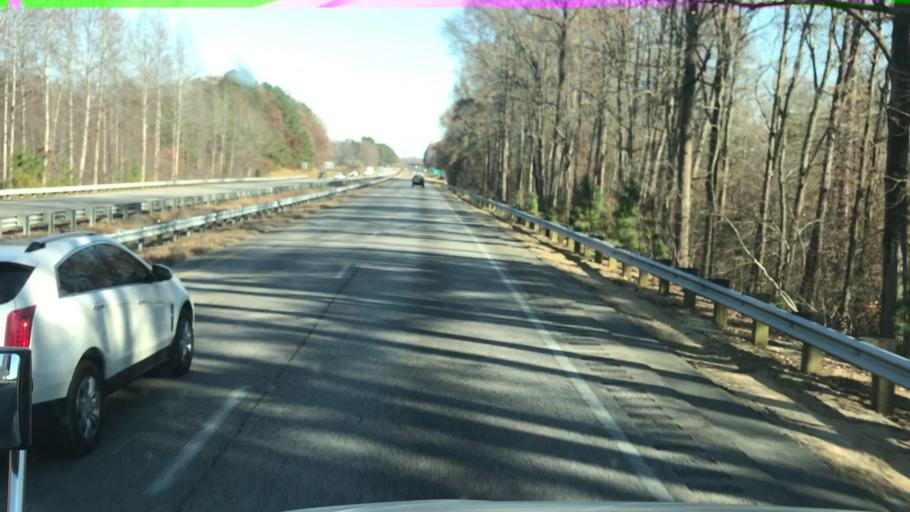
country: US
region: North Carolina
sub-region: Nash County
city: Nashville
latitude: 35.9775
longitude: -77.9093
